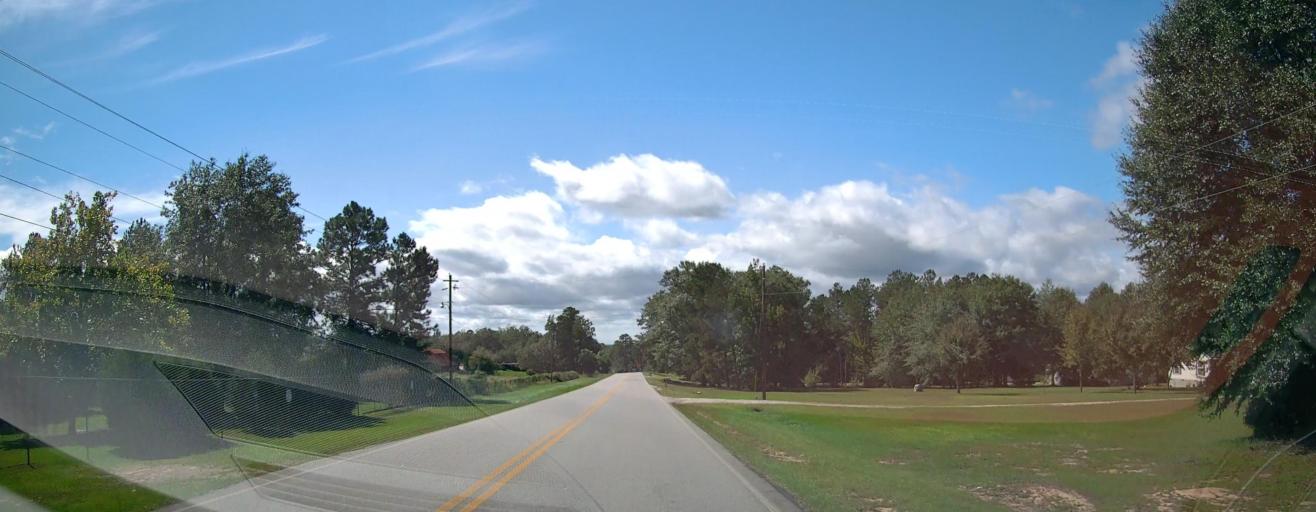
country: US
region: Georgia
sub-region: Houston County
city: Warner Robins
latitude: 32.7112
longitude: -83.5420
